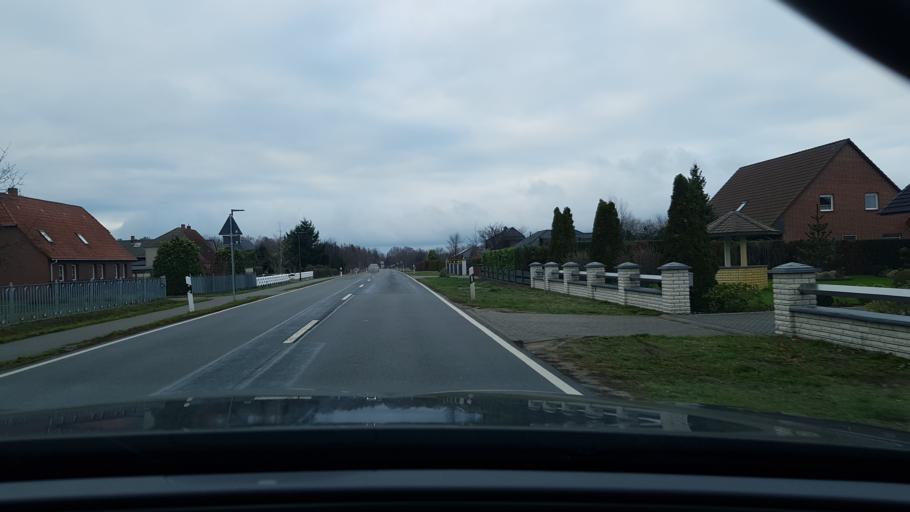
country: DE
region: Saxony-Anhalt
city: Oebisfelde
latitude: 52.4216
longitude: 11.0140
